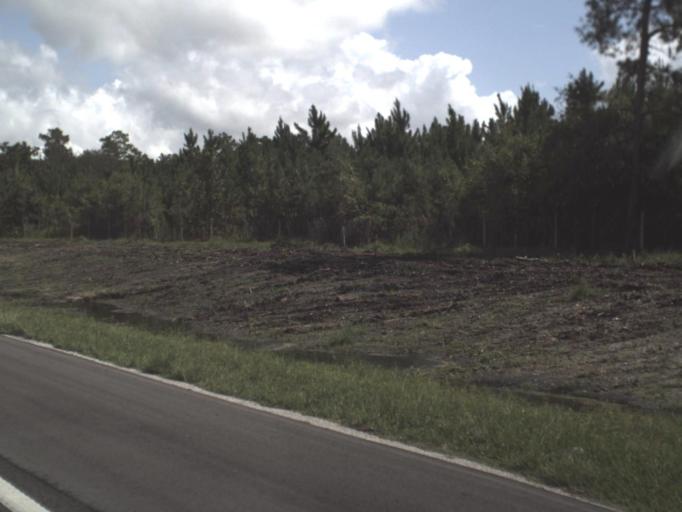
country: US
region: Florida
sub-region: Pasco County
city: San Antonio
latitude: 28.3724
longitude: -82.3194
